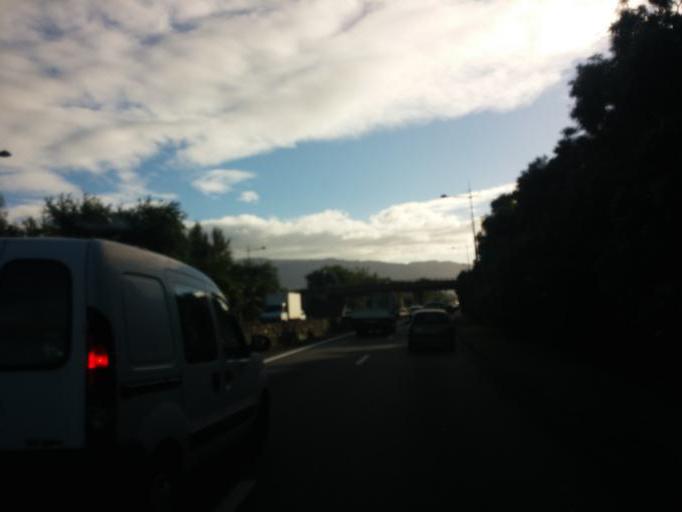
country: RE
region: Reunion
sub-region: Reunion
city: Saint-Denis
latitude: -20.8868
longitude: 55.4906
